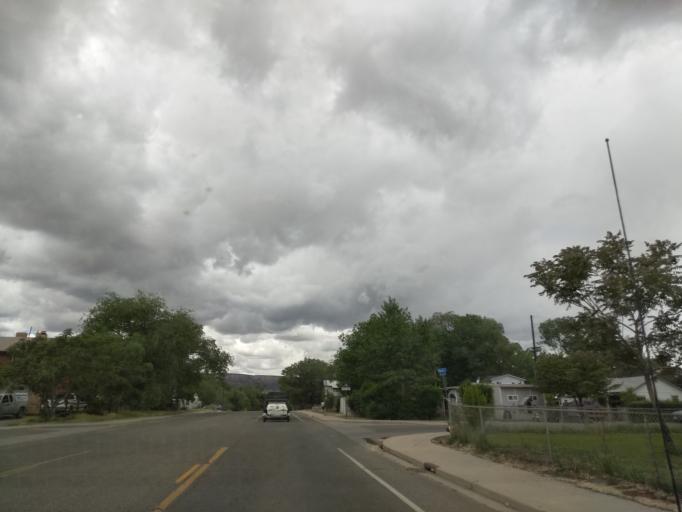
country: US
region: Colorado
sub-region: Mesa County
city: Orchard Mesa
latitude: 39.0486
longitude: -108.5606
